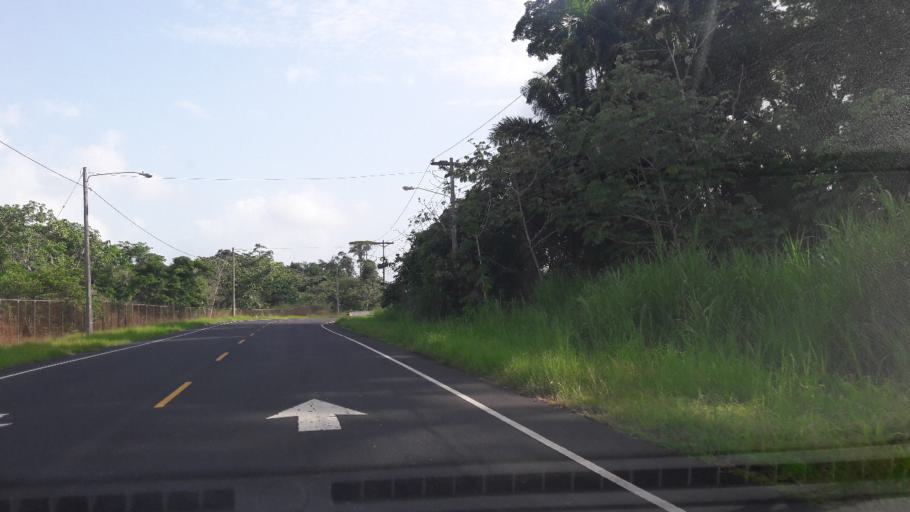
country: PA
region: Colon
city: Cativa
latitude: 9.3557
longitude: -79.8630
